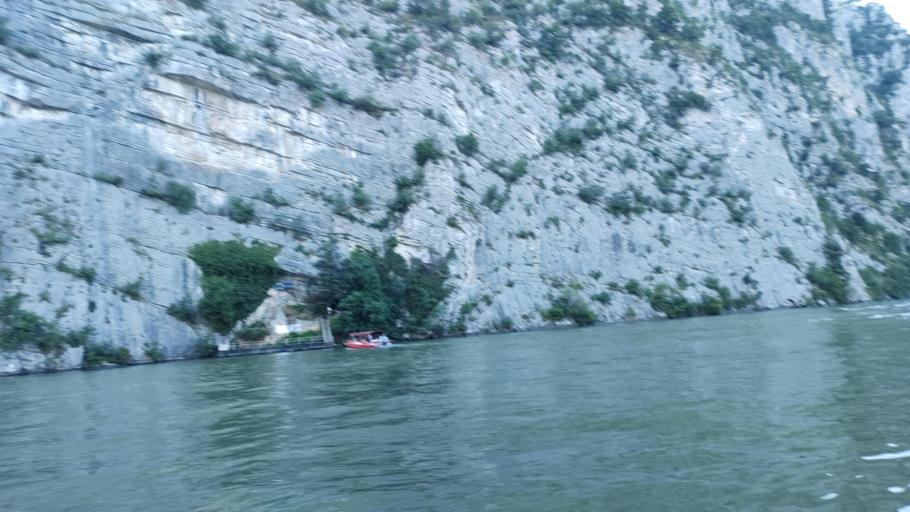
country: RO
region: Mehedinti
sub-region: Comuna Dubova
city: Dubova
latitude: 44.5986
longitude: 22.2642
